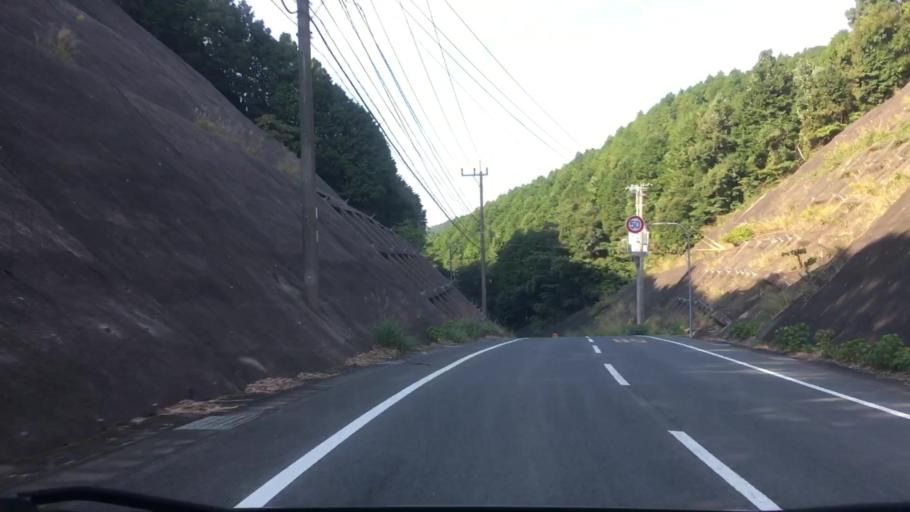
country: JP
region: Nagasaki
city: Sasebo
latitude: 32.9691
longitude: 129.6962
